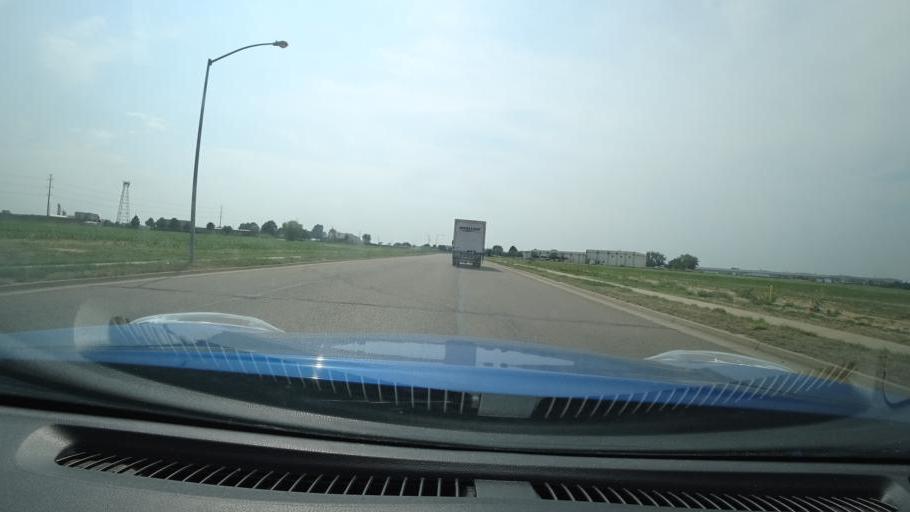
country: US
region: Colorado
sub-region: Adams County
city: Aurora
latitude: 39.7568
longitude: -104.7368
